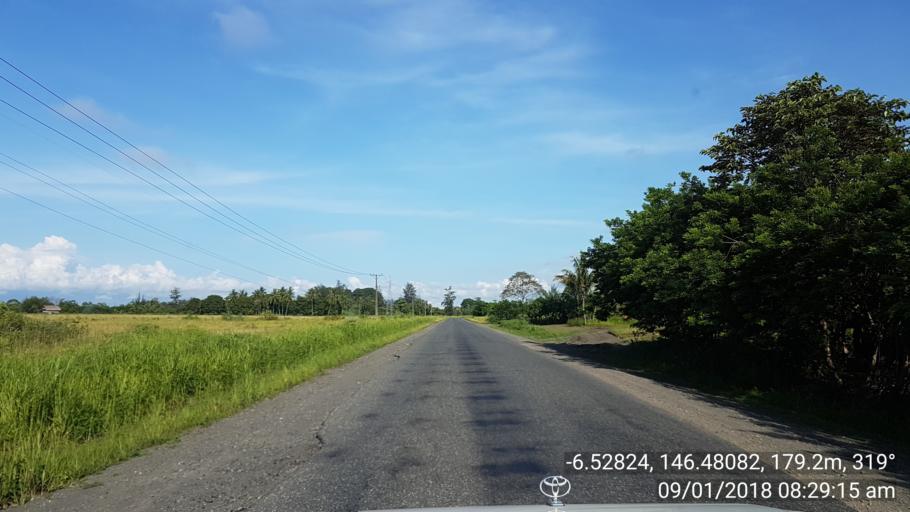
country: PG
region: Morobe
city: Lae
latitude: -6.5285
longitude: 146.4812
